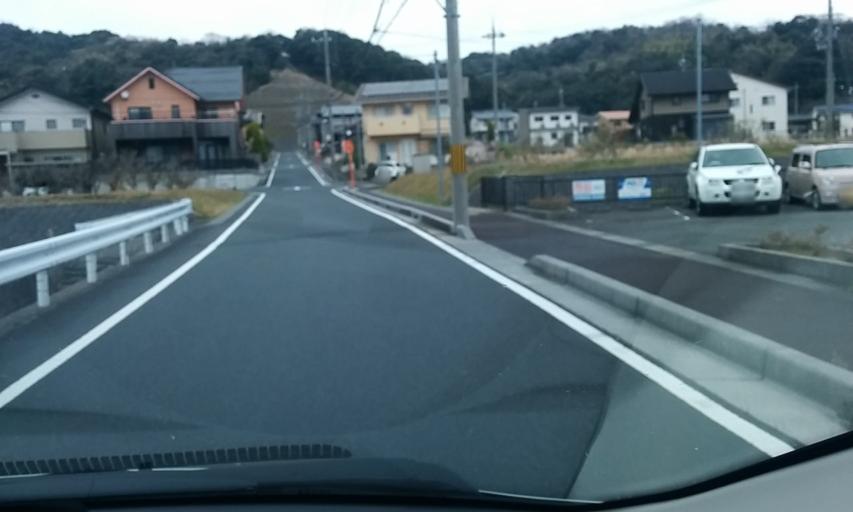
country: JP
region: Kyoto
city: Miyazu
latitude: 35.5533
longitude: 135.2102
